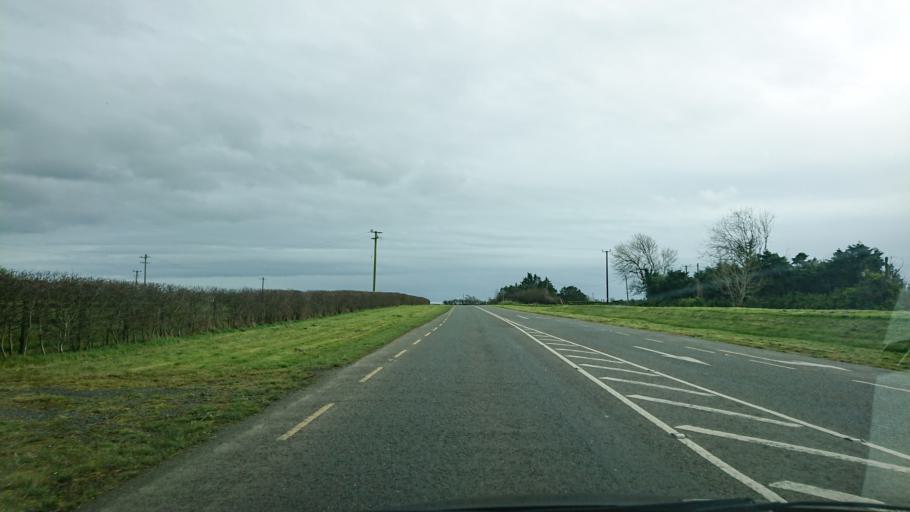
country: IE
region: Munster
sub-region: Waterford
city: Waterford
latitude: 52.2019
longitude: -7.0809
